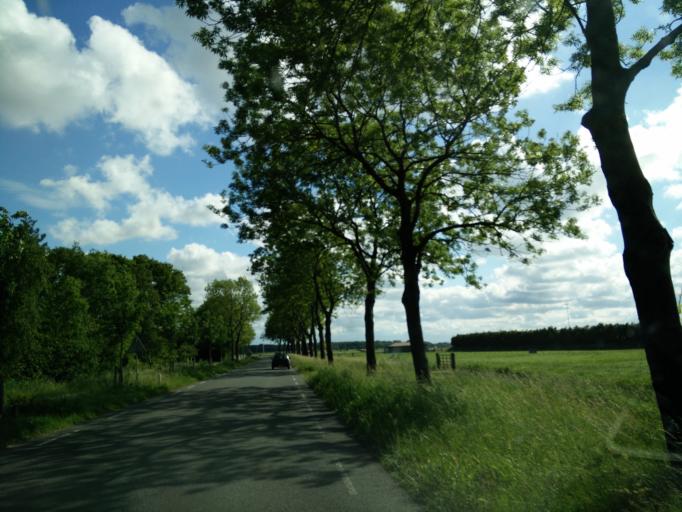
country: NL
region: Groningen
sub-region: Gemeente Groningen
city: Korrewegwijk
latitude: 53.2631
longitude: 6.5893
